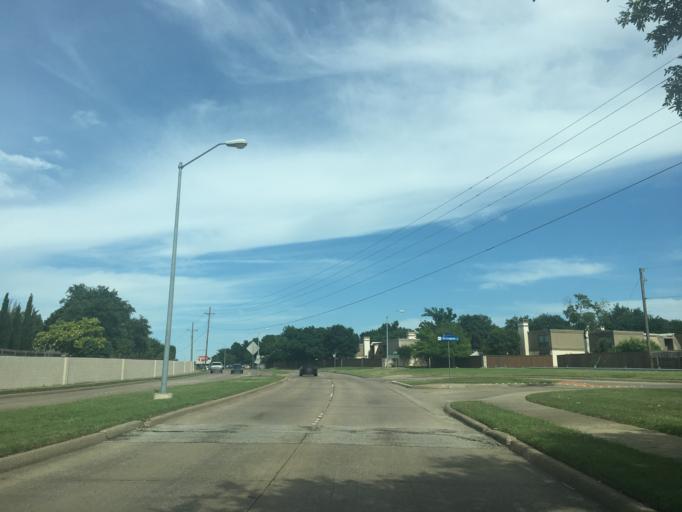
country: US
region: Texas
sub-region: Dallas County
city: Richardson
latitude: 32.9316
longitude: -96.7065
